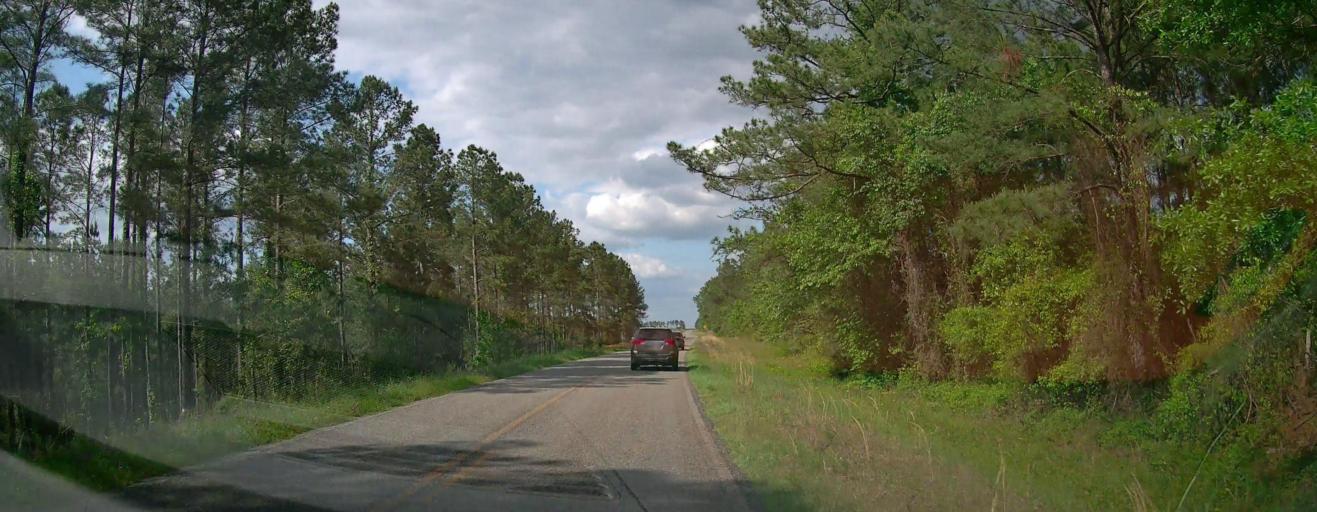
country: US
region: Georgia
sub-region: Laurens County
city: East Dublin
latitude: 32.7081
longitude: -82.9183
